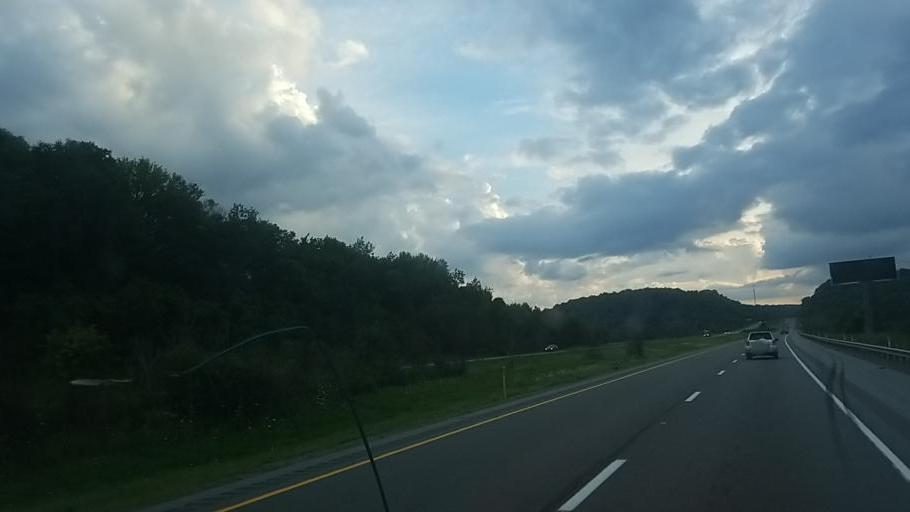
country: US
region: Pennsylvania
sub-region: Clearfield County
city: Treasure Lake
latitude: 41.1229
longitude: -78.6096
